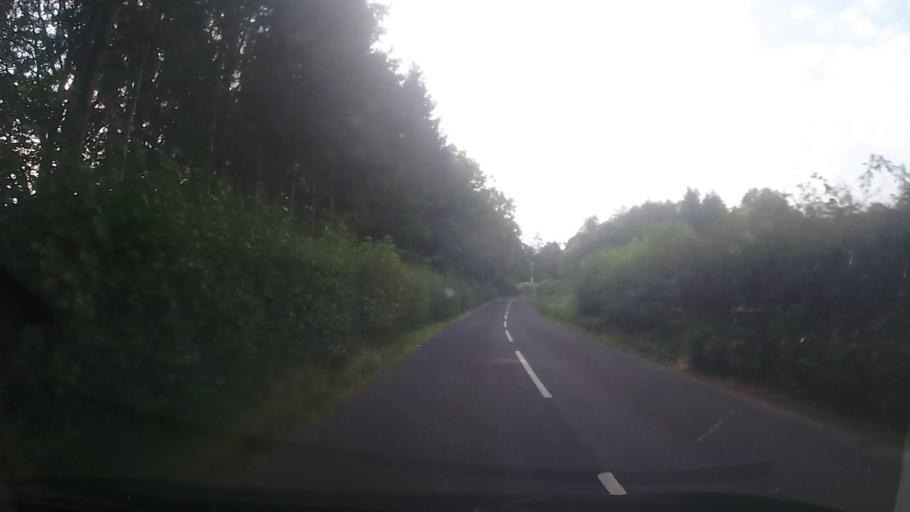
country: GB
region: Wales
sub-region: Sir Powys
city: Rhayader
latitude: 52.2844
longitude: -3.5475
